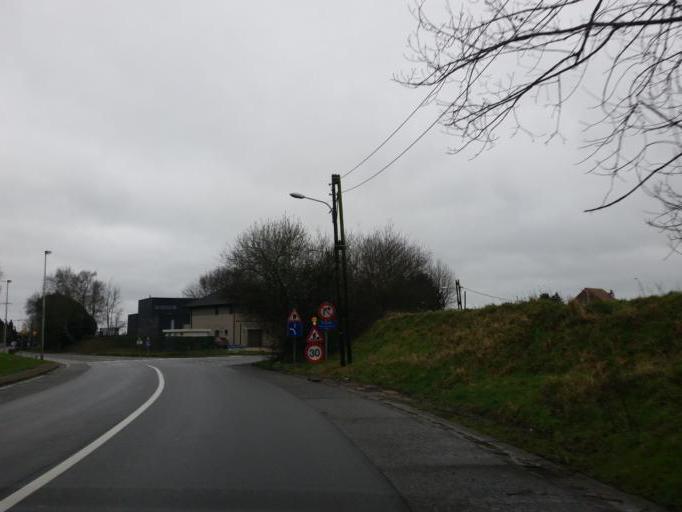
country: BE
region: Flanders
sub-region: Provincie Vlaams-Brabant
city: Vilvoorde
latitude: 50.9425
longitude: 4.4053
